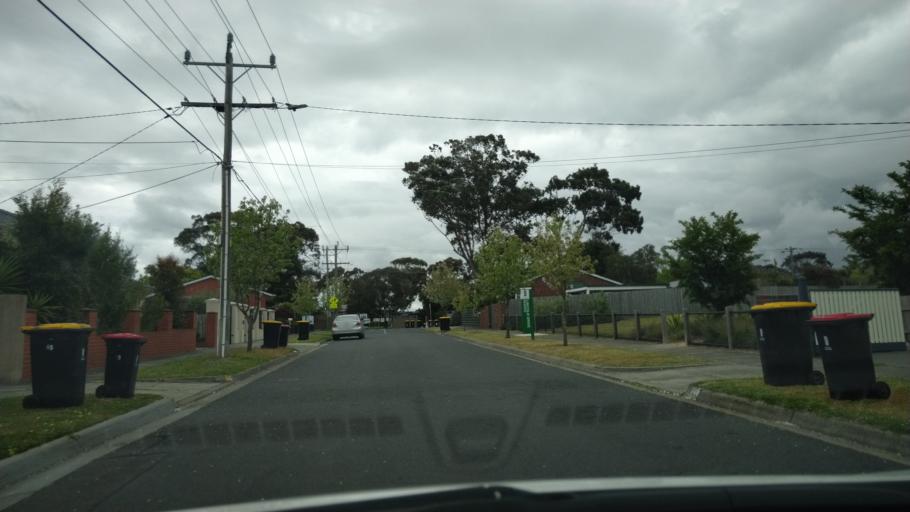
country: AU
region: Victoria
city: Heatherton
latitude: -37.9634
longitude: 145.0790
